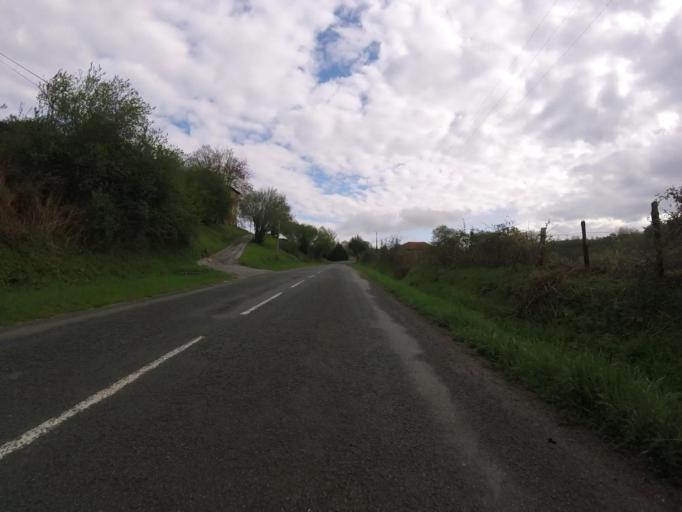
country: FR
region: Aquitaine
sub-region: Departement des Pyrenees-Atlantiques
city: Sare
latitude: 43.2963
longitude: -1.5911
